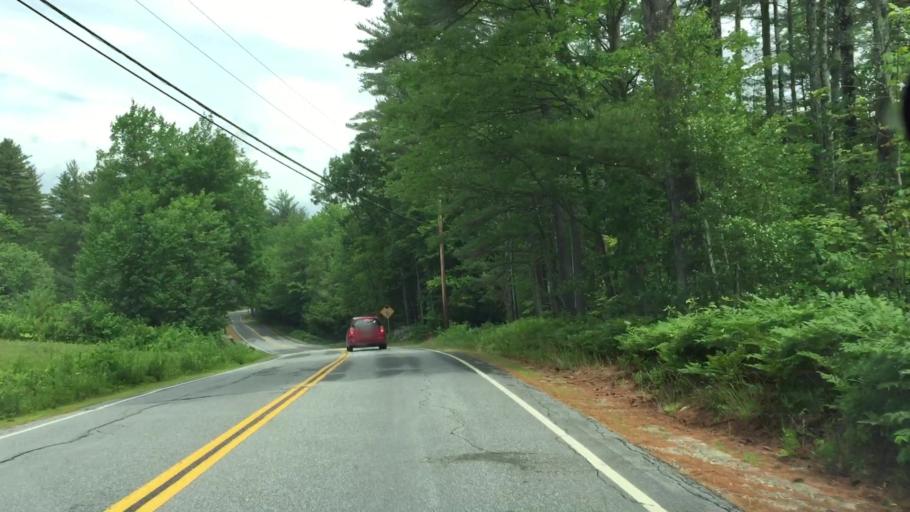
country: US
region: New Hampshire
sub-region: Carroll County
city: Sandwich
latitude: 43.8007
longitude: -71.4428
